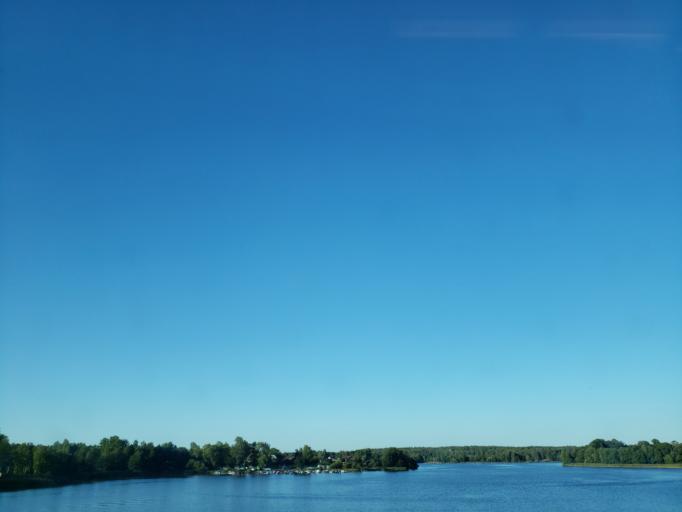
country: RU
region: Leningrad
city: Vyborg
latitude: 60.7183
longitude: 28.7398
